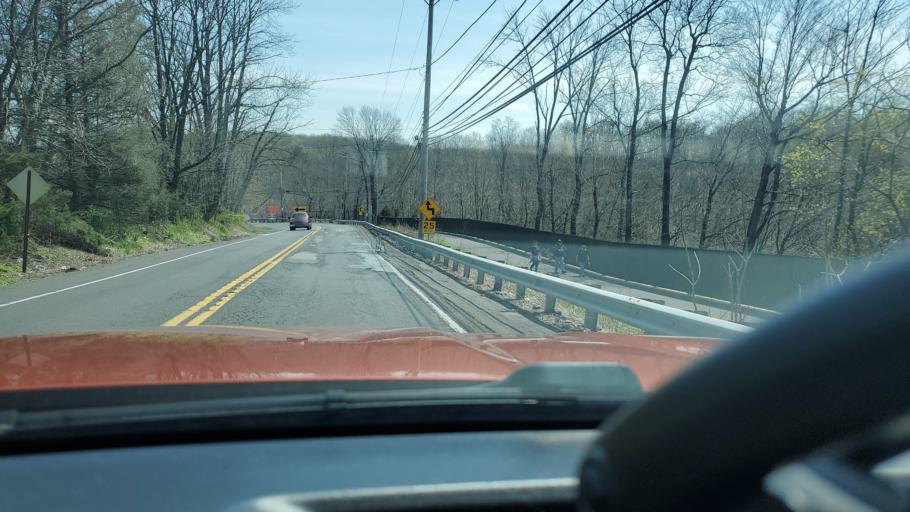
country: US
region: Pennsylvania
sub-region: Montgomery County
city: Red Hill
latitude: 40.3421
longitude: -75.4776
